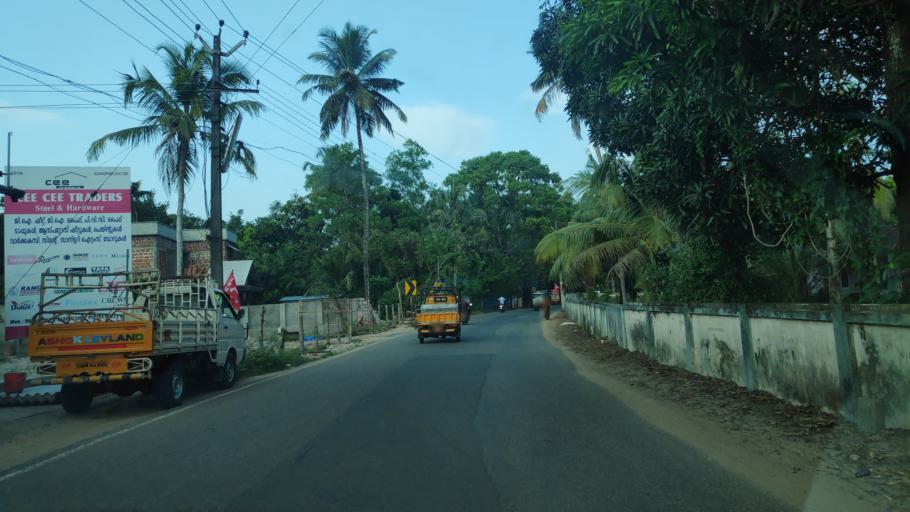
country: IN
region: Kerala
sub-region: Alappuzha
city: Alleppey
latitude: 9.5793
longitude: 76.3491
